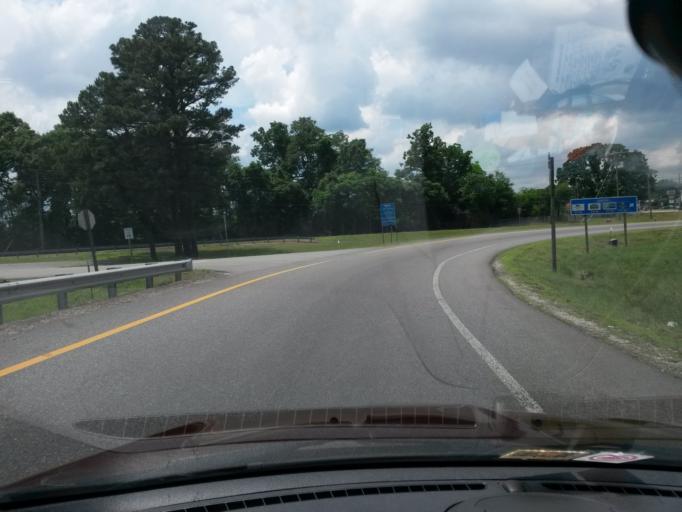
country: US
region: Virginia
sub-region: Chesterfield County
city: Chester
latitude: 37.3529
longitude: -77.4062
